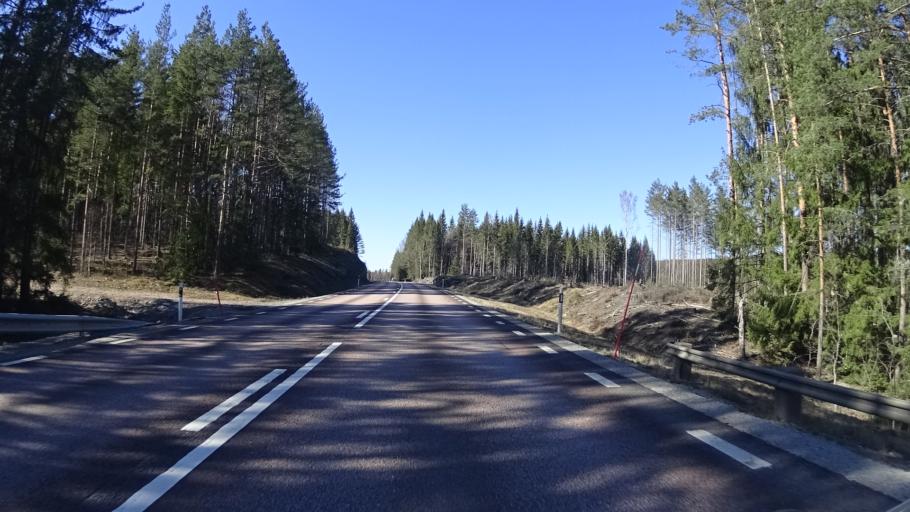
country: SE
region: Vaermland
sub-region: Karlstads Kommun
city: Edsvalla
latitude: 59.6039
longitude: 12.9968
